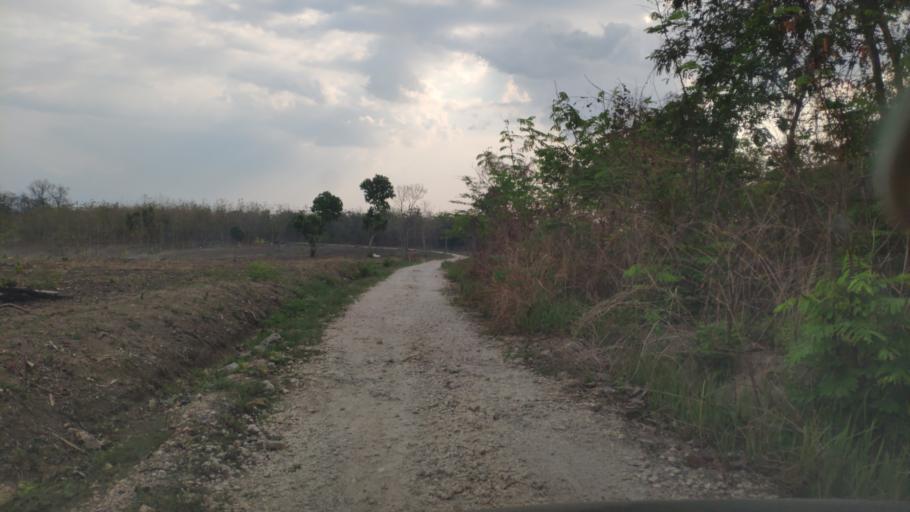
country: ID
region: Central Java
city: Randublatung
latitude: -7.2768
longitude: 111.2847
